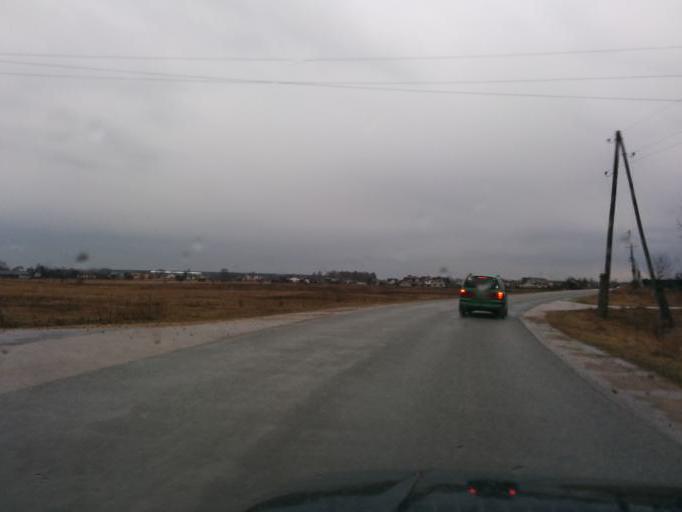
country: LV
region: Kekava
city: Balozi
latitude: 56.8943
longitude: 24.1754
